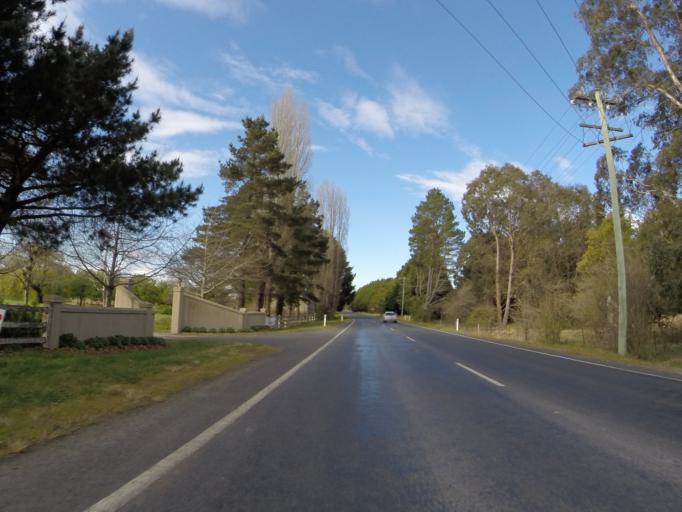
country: AU
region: New South Wales
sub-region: Wingecarribee
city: Moss Vale
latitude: -34.5783
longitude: 150.3065
